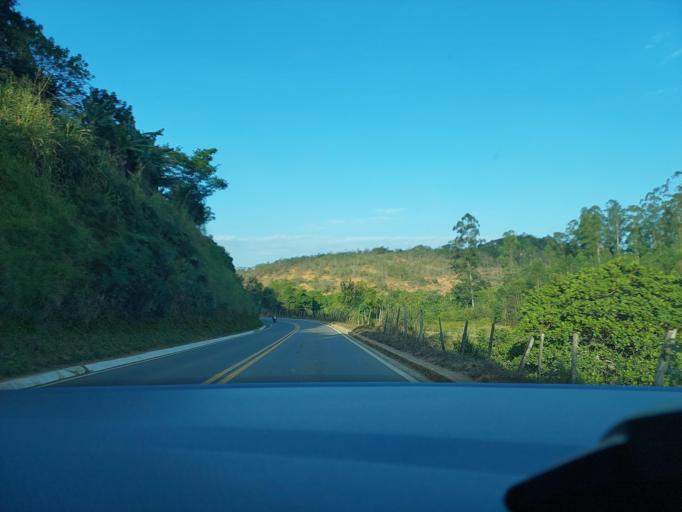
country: BR
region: Minas Gerais
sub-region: Muriae
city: Muriae
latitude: -21.1102
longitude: -42.4543
